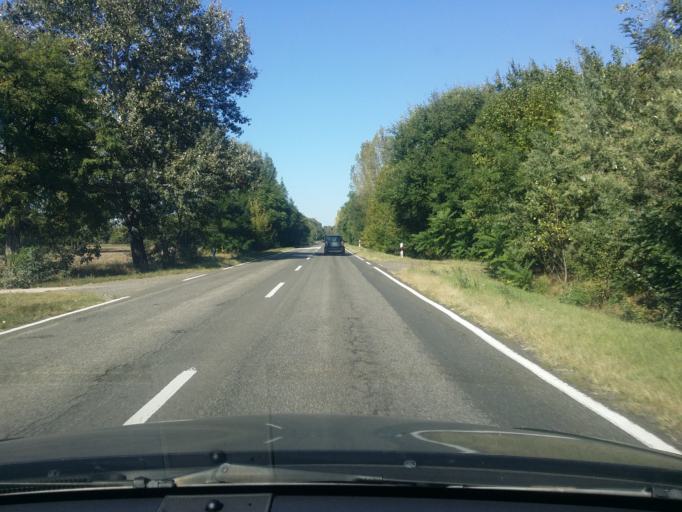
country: HU
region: Bacs-Kiskun
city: Palmonostora
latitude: 46.5817
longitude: 19.9294
